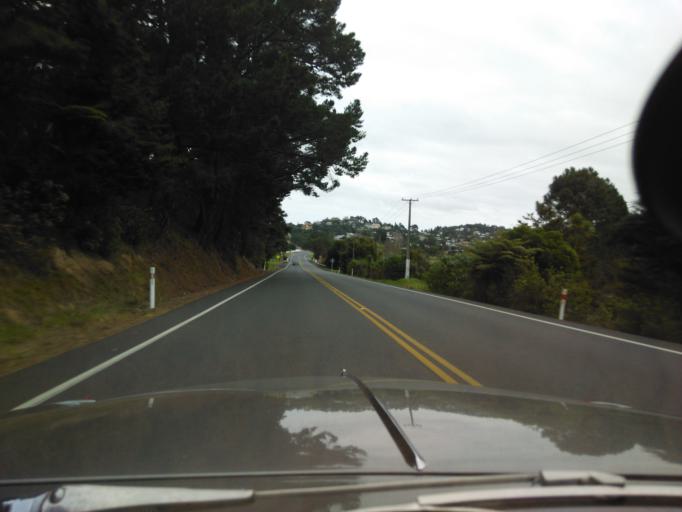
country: NZ
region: Auckland
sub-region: Auckland
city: Warkworth
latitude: -36.5595
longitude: 174.6971
